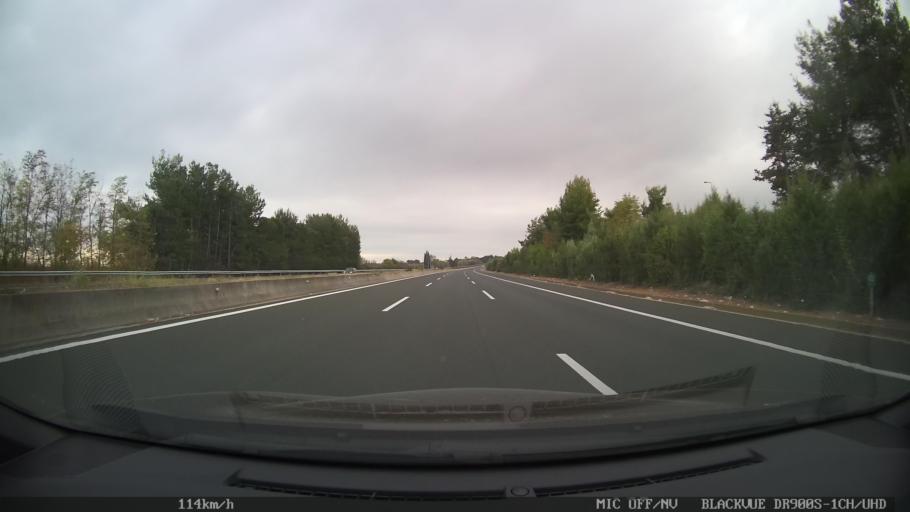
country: GR
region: Central Macedonia
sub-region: Nomos Pierias
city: Makrygialos
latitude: 40.3920
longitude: 22.6039
